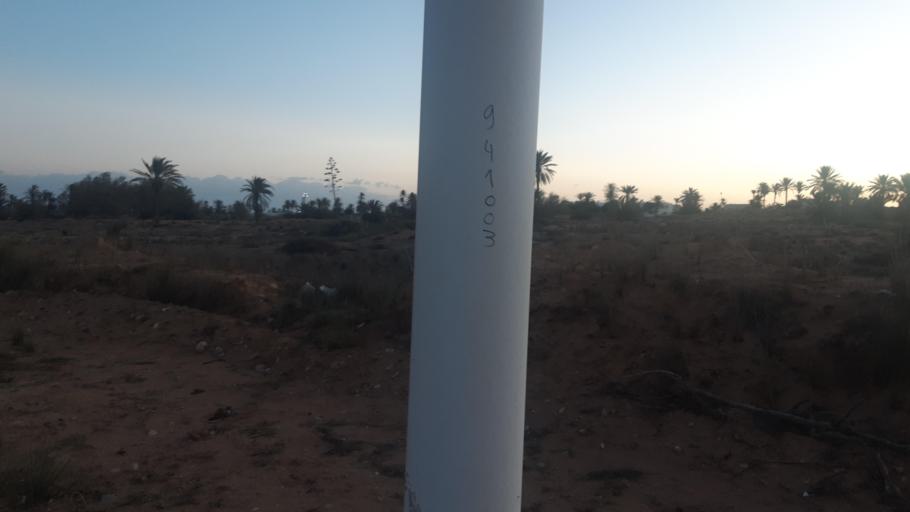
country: TN
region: Madanin
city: Midoun
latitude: 33.7999
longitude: 11.0472
